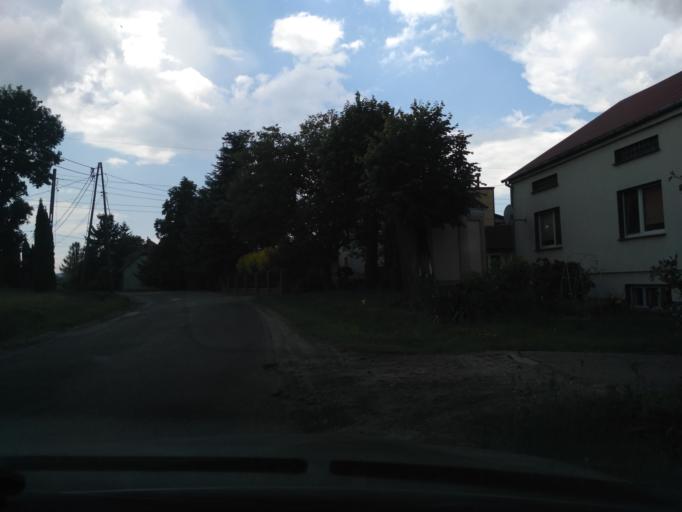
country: PL
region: Subcarpathian Voivodeship
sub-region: Powiat lancucki
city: Wysoka
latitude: 50.0393
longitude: 22.2450
